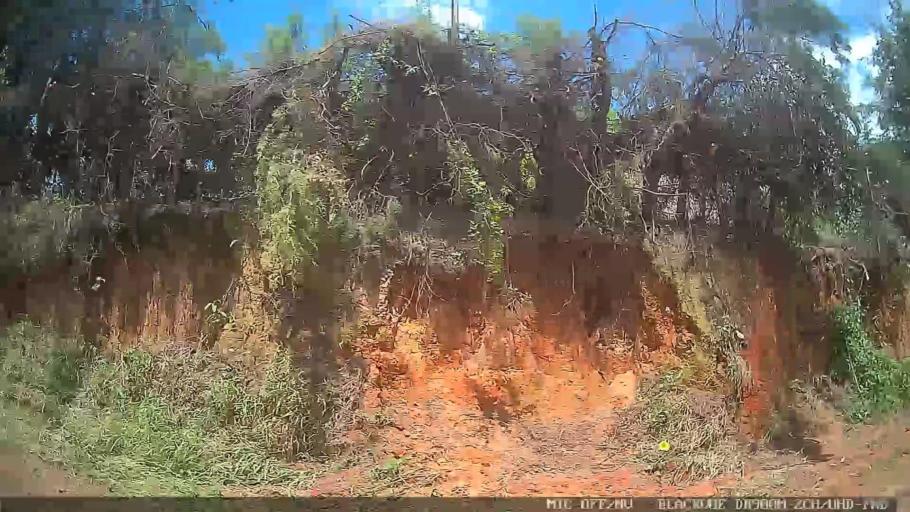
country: BR
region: Minas Gerais
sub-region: Extrema
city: Extrema
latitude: -22.7525
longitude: -46.4351
